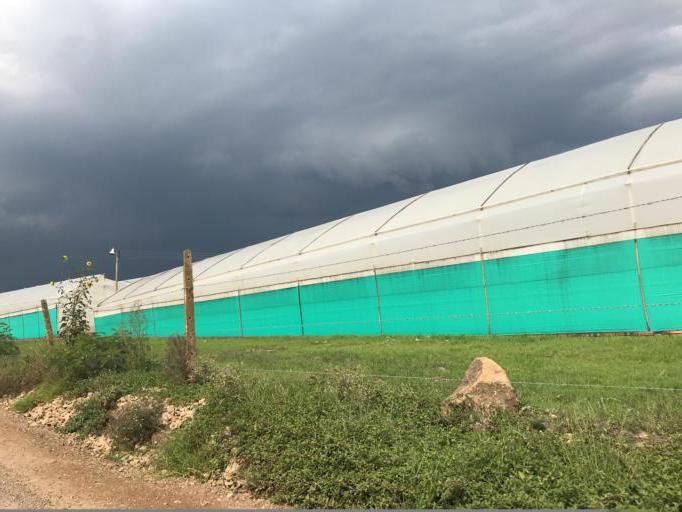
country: CO
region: Boyaca
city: Villa de Leiva
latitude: 5.6594
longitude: -73.5854
